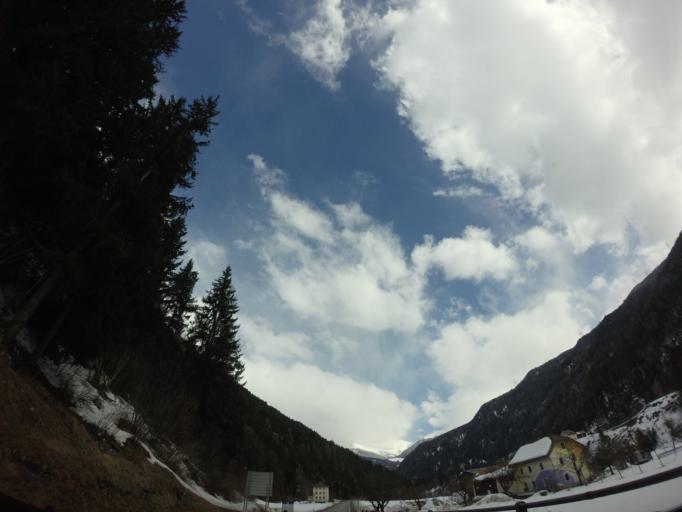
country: AT
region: Tyrol
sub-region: Politischer Bezirk Landeck
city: Nauders
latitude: 46.8672
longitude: 10.4409
